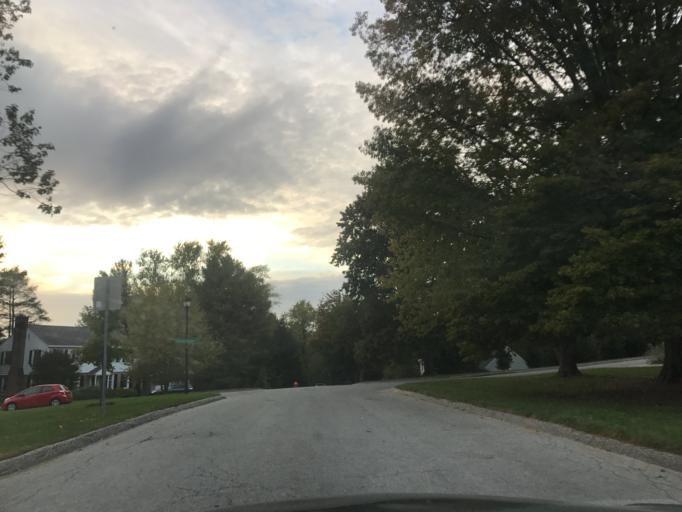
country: US
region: Maryland
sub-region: Baltimore County
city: Lutherville
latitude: 39.4069
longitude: -76.6347
